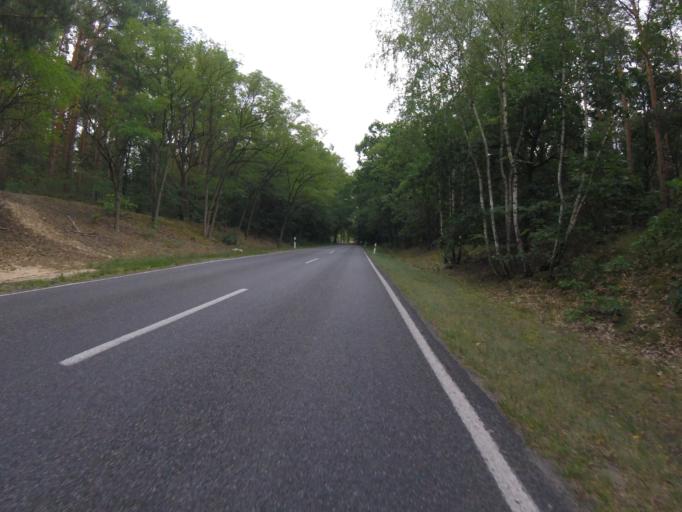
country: DE
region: Brandenburg
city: Halbe
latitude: 52.0973
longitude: 13.7097
